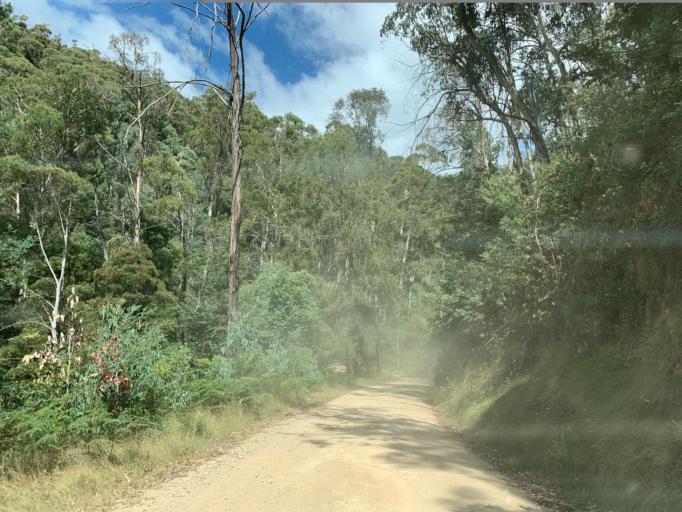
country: AU
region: Victoria
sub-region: Mansfield
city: Mansfield
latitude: -37.0935
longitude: 146.5185
